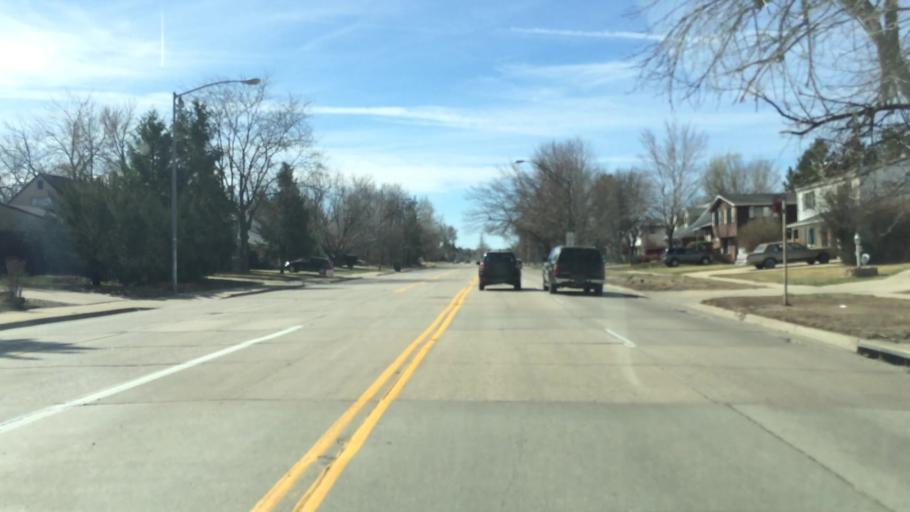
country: US
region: Colorado
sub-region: Arapahoe County
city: Glendale
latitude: 39.6856
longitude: -104.9129
